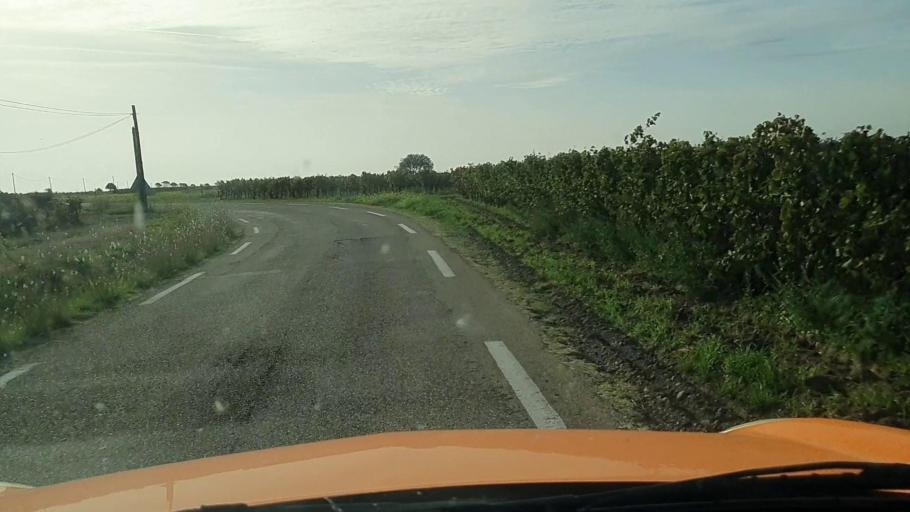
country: FR
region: Languedoc-Roussillon
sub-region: Departement du Gard
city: Beauvoisin
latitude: 43.7076
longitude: 4.3402
